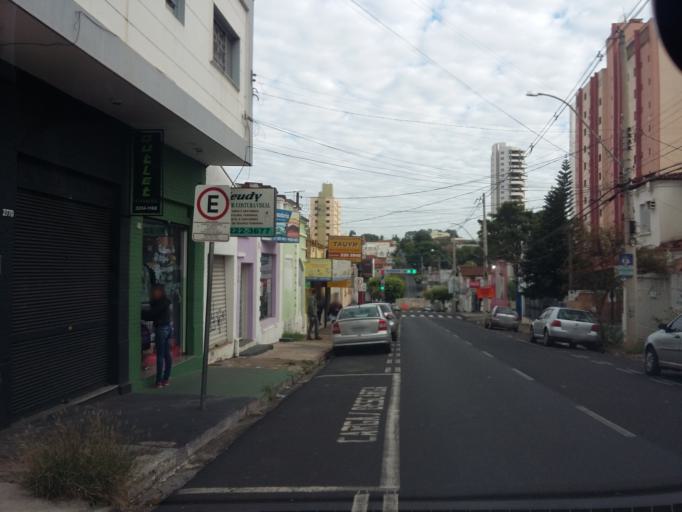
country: BR
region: Sao Paulo
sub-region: Sao Jose Do Rio Preto
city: Sao Jose do Rio Preto
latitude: -20.8119
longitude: -49.3843
